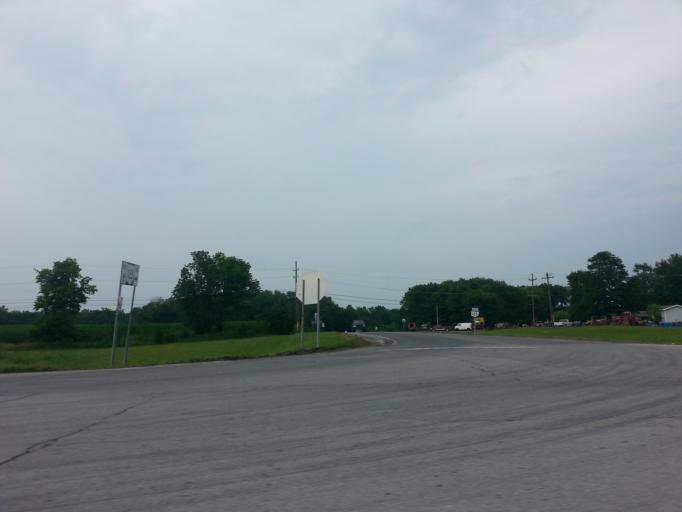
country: US
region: Ohio
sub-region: Brown County
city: Georgetown
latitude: 38.8551
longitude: -83.8555
